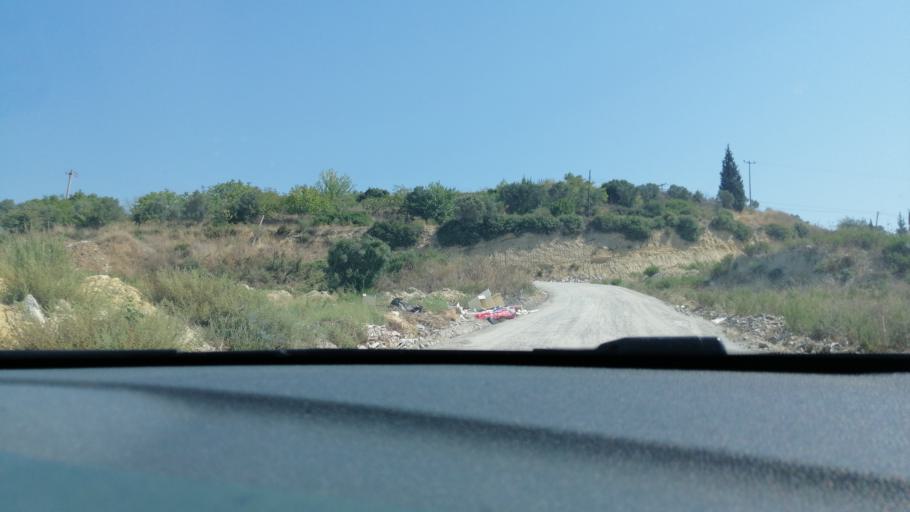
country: TR
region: Aydin
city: Davutlar
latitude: 37.7843
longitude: 27.3156
